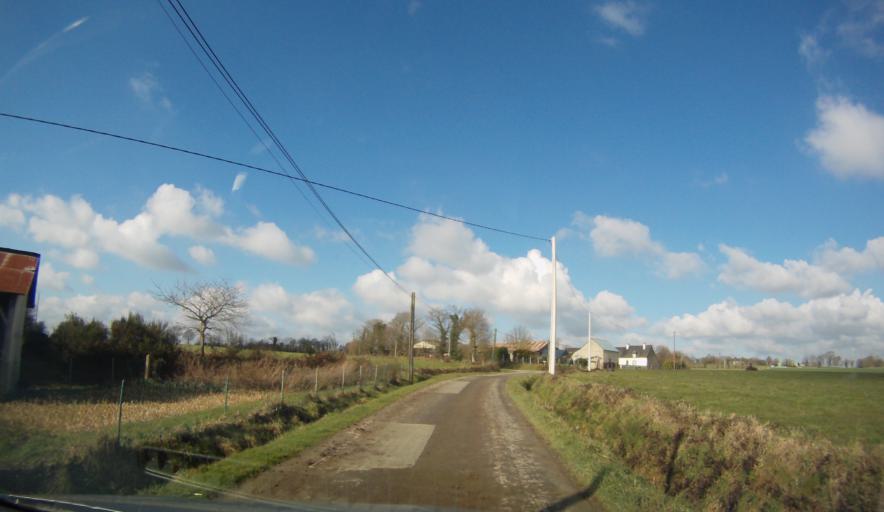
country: FR
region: Brittany
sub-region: Departement d'Ille-et-Vilaine
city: Corps-Nuds
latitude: 47.9523
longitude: -1.5586
